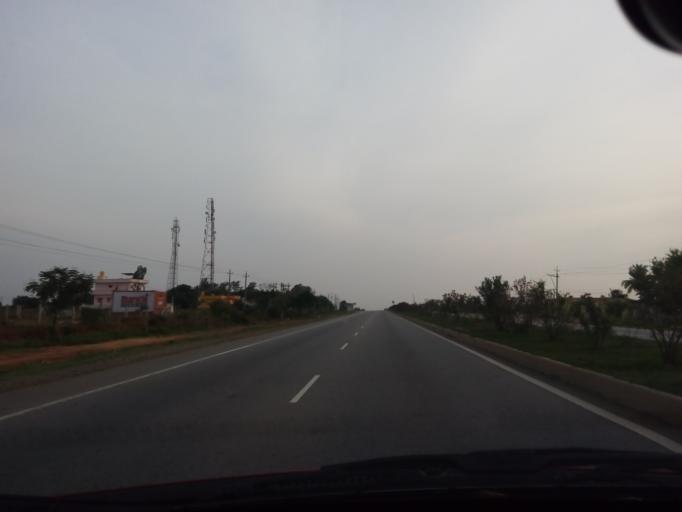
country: IN
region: Karnataka
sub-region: Chikkaballapur
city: Chik Ballapur
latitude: 13.5249
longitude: 77.7651
